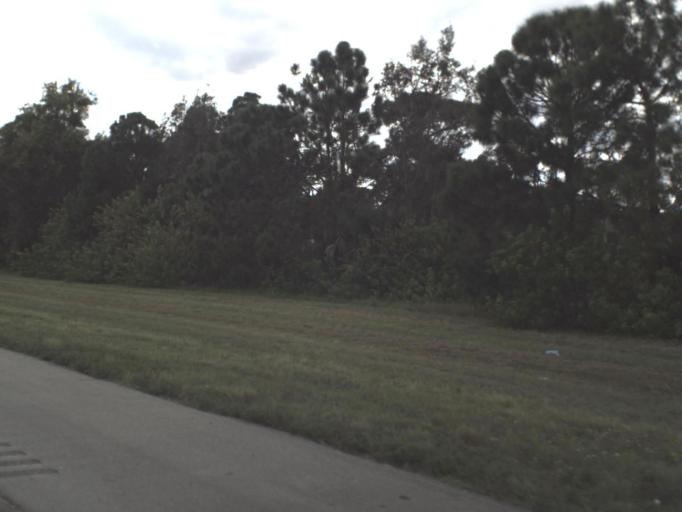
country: US
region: Florida
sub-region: Saint Lucie County
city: River Park
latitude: 27.3419
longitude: -80.3743
